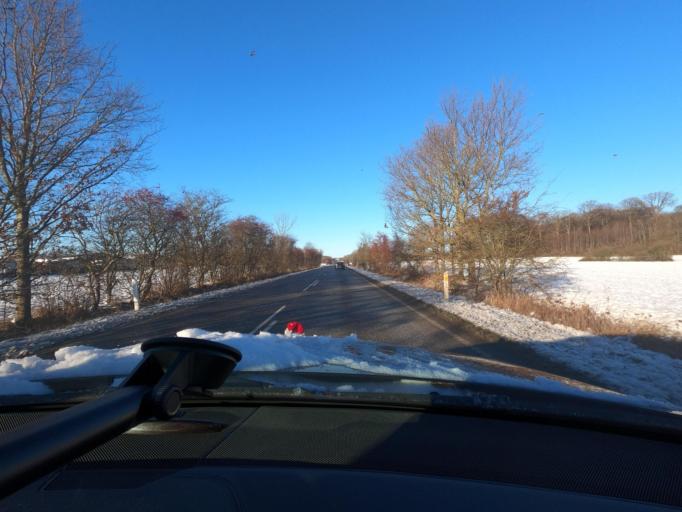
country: DK
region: South Denmark
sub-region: Sonderborg Kommune
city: Horuphav
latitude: 54.9140
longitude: 9.9107
